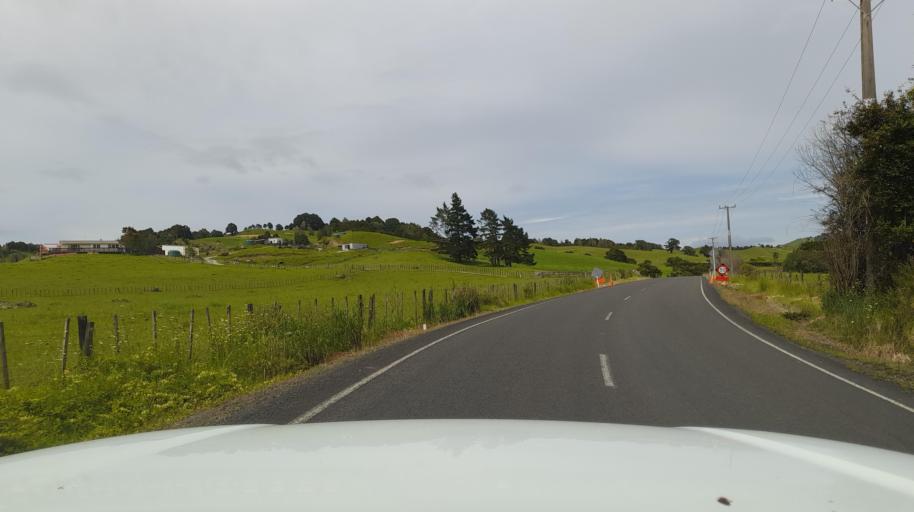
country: NZ
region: Northland
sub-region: Far North District
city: Taipa
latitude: -35.2684
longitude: 173.4966
